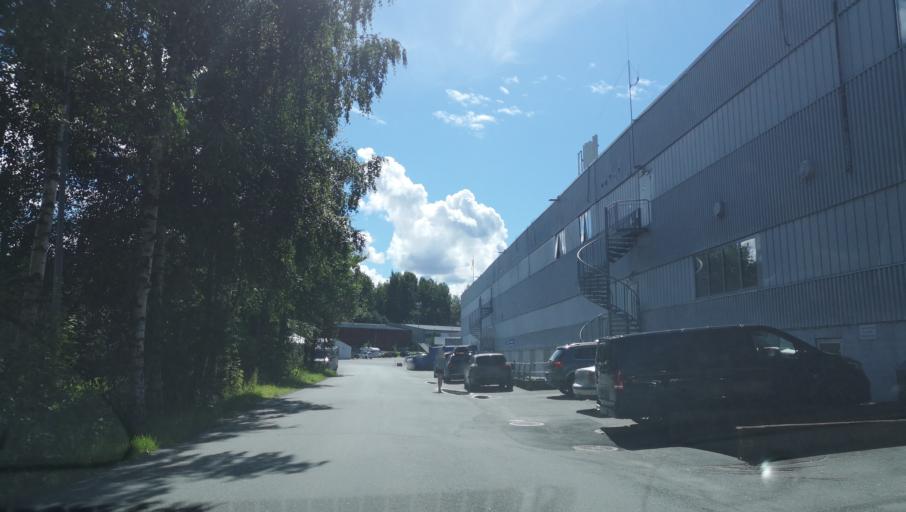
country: NO
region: Akershus
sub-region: Frogn
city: Drobak
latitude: 59.6731
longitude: 10.6587
